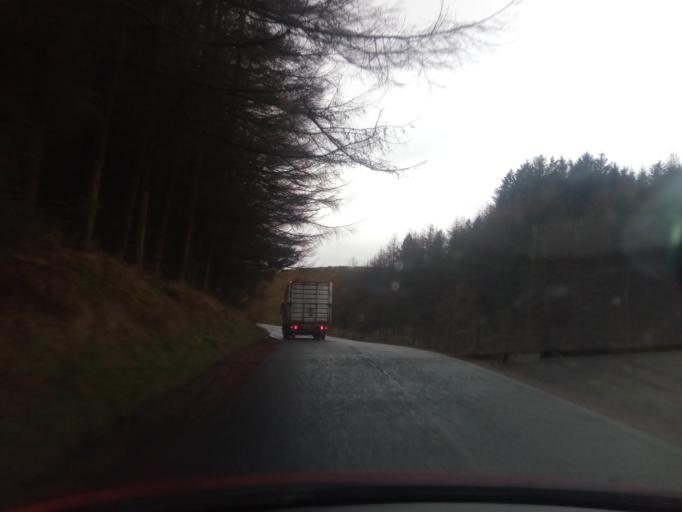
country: GB
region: Scotland
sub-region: The Scottish Borders
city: Hawick
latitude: 55.2713
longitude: -2.6895
